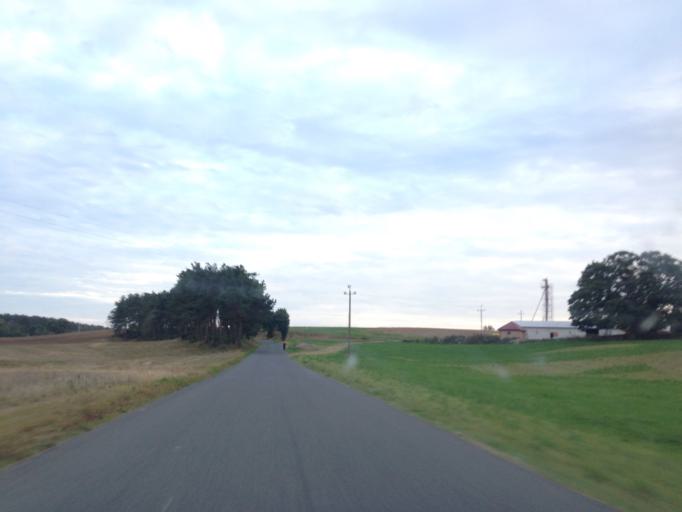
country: PL
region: Kujawsko-Pomorskie
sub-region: Powiat brodnicki
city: Brzozie
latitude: 53.2953
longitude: 19.6896
